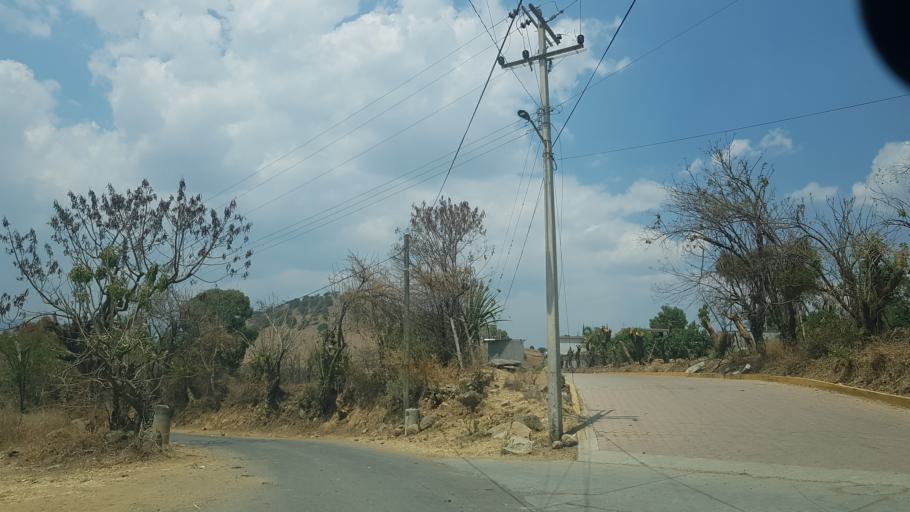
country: MX
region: Puebla
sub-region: Atzitzihuacan
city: Santiago Atzitzihuacan
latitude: 18.8081
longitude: -98.6229
